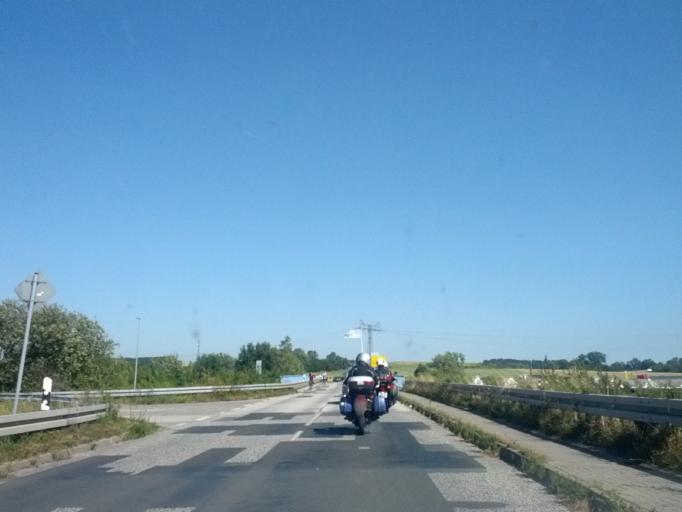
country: DE
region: Mecklenburg-Vorpommern
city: Sagard
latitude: 54.4901
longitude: 13.5790
